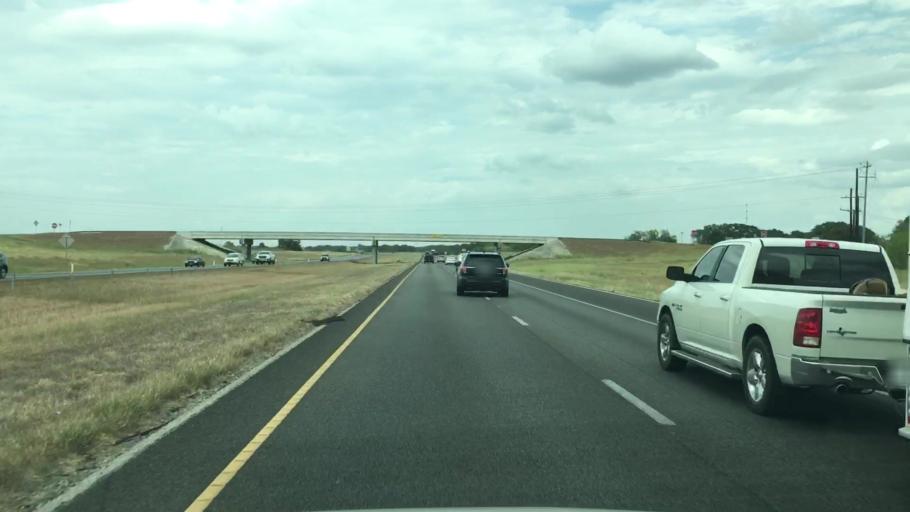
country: US
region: Texas
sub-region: Bexar County
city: Elmendorf
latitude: 29.1399
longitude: -98.4289
